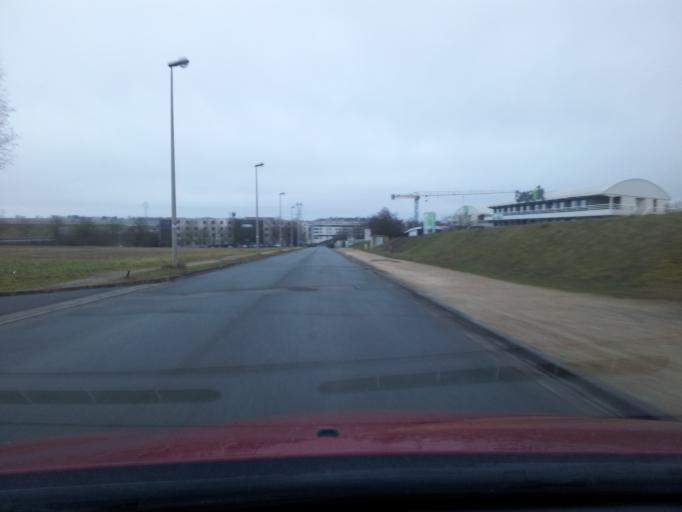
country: FR
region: Poitou-Charentes
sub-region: Departement de la Vienne
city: Chasseneuil-du-Poitou
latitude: 46.6642
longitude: 0.3578
